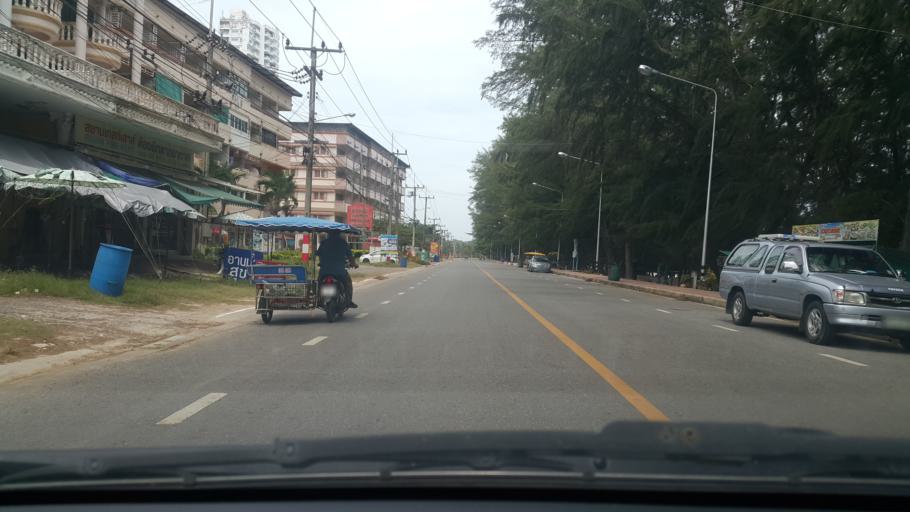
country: TH
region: Rayong
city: Rayong
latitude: 12.6140
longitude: 101.3799
